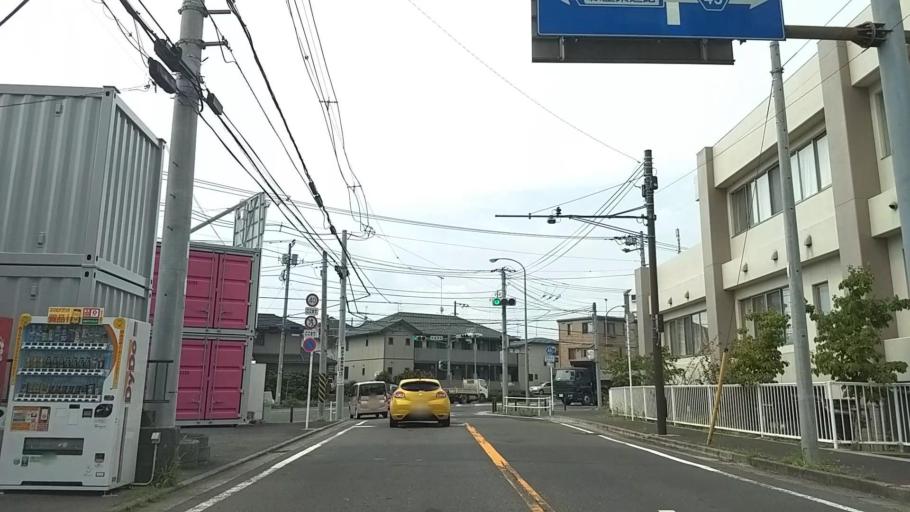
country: JP
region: Kanagawa
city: Yokohama
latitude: 35.5142
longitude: 139.5578
